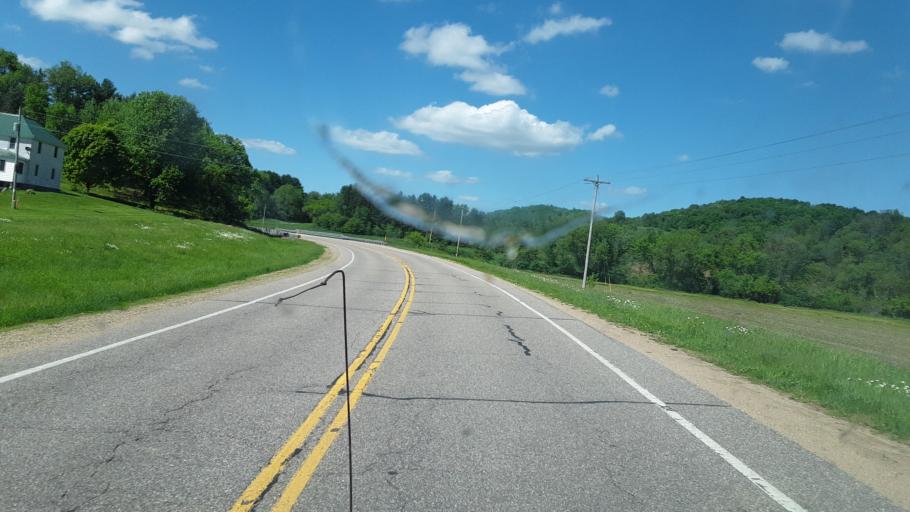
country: US
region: Wisconsin
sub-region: Richland County
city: Richland Center
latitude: 43.4281
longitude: -90.2413
